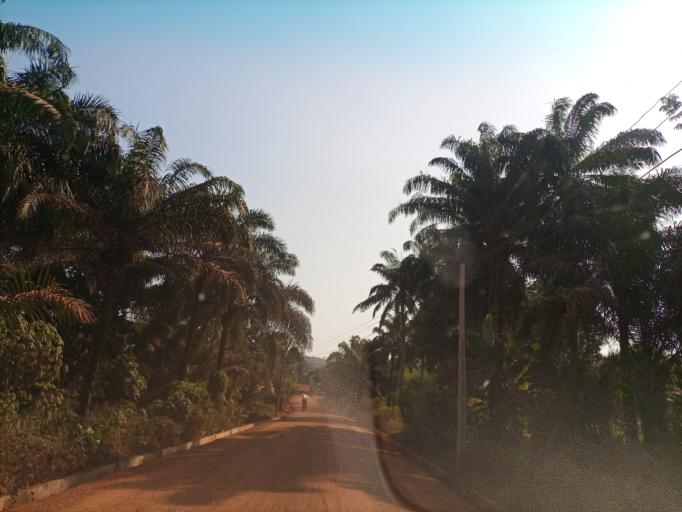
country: NG
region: Enugu
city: Aku
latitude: 6.7035
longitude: 7.3211
